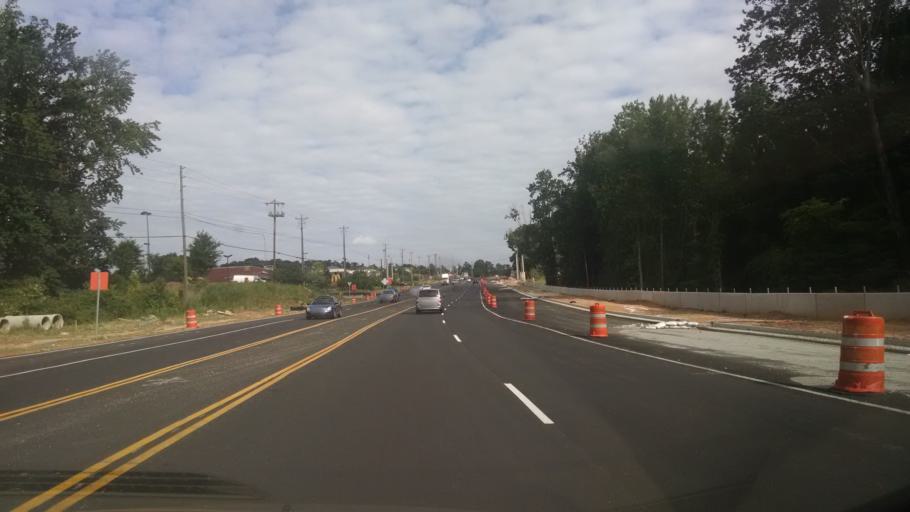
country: US
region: Georgia
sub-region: Gwinnett County
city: Sugar Hill
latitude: 34.1228
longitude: -84.0810
